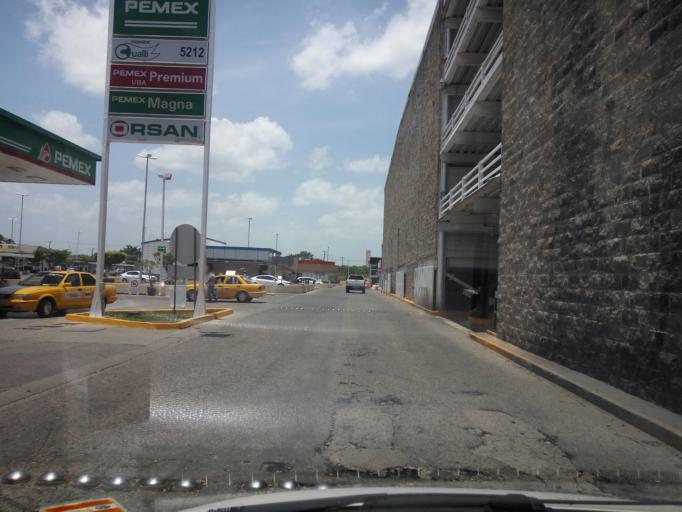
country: MX
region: Tabasco
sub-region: Nacajuca
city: Brisas del Carrizal
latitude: 17.9896
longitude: -92.9644
